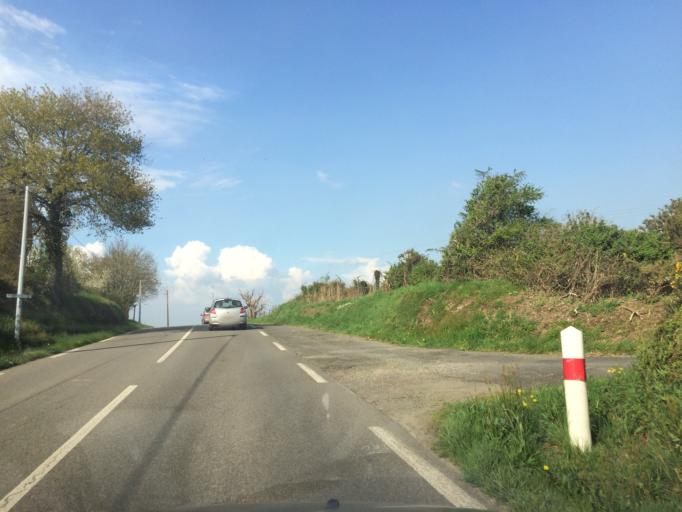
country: FR
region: Pays de la Loire
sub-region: Departement de la Loire-Atlantique
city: Suce-sur-Erdre
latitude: 47.3186
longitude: -1.5106
